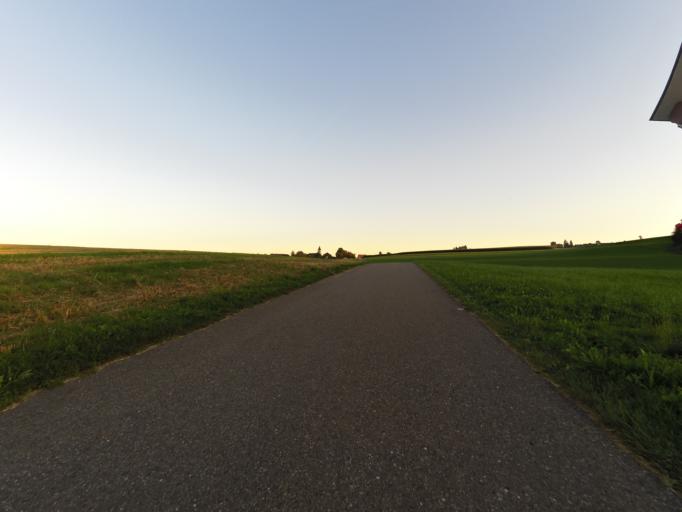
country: CH
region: Thurgau
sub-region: Weinfelden District
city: Wigoltingen
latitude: 47.5702
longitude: 9.0331
